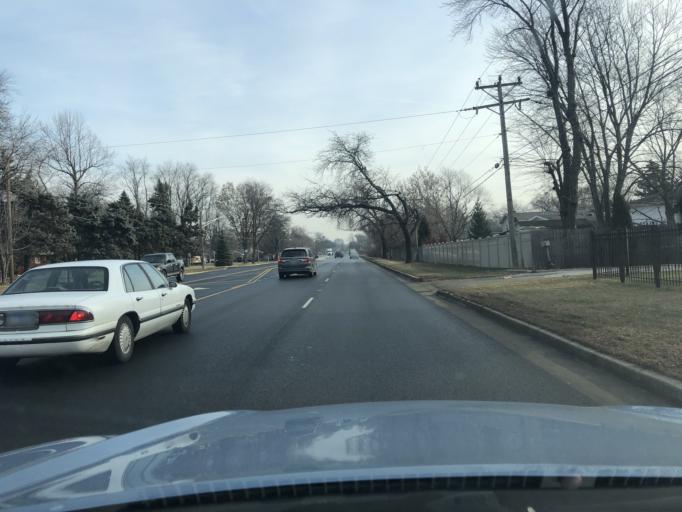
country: US
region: Illinois
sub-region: Cook County
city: Mount Prospect
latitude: 42.0477
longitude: -87.9340
